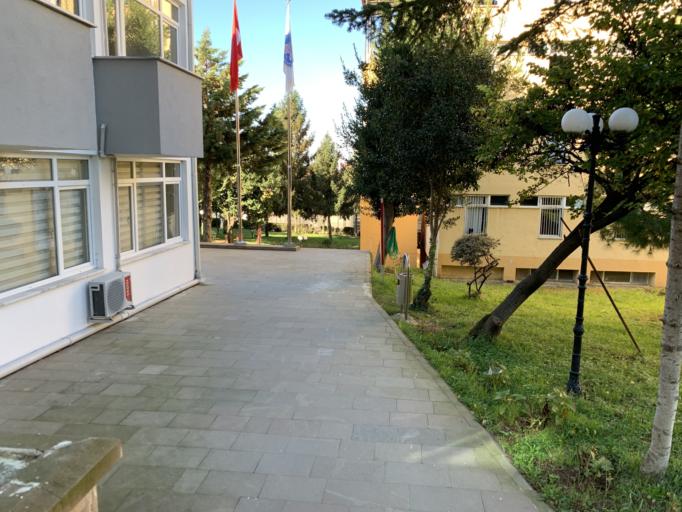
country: TR
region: Trabzon
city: Trabzon
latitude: 40.9956
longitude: 39.7696
